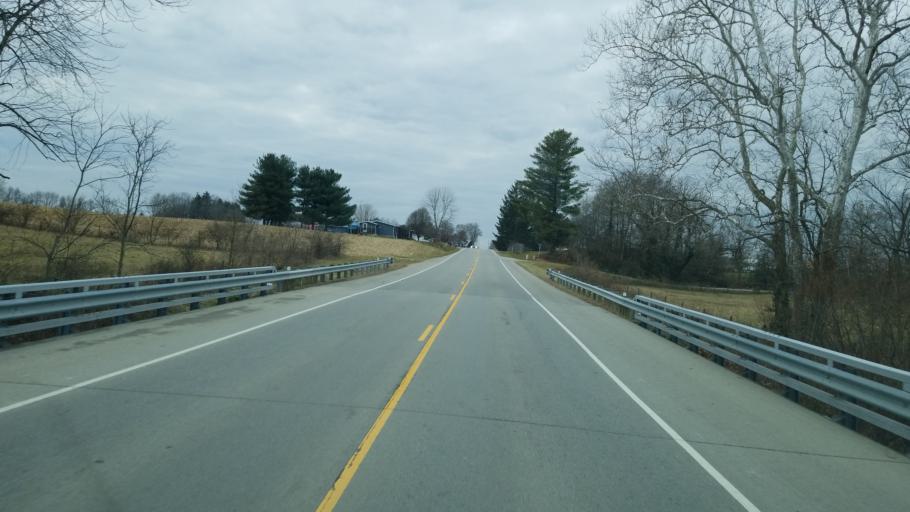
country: US
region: Ohio
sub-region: Highland County
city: Greenfield
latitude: 39.2187
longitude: -83.4306
